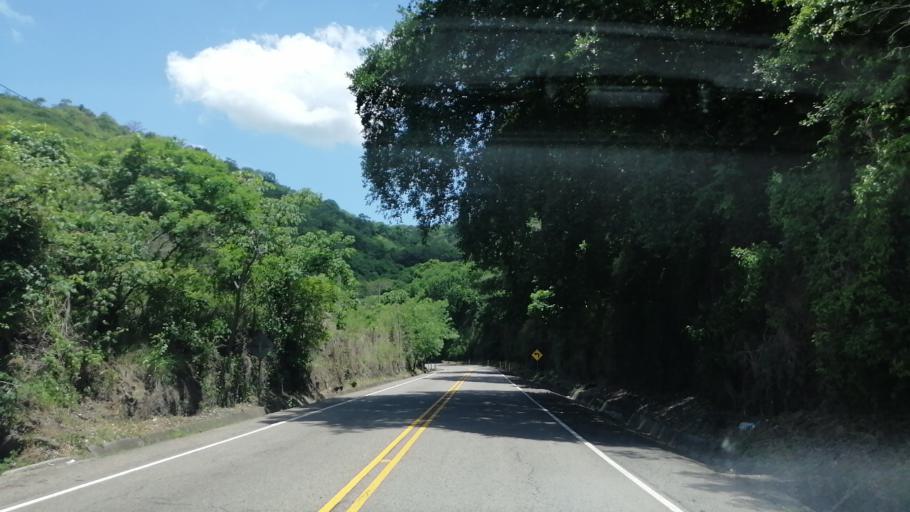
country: SV
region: Chalatenango
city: Nueva Concepcion
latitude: 14.1633
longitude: -89.3120
